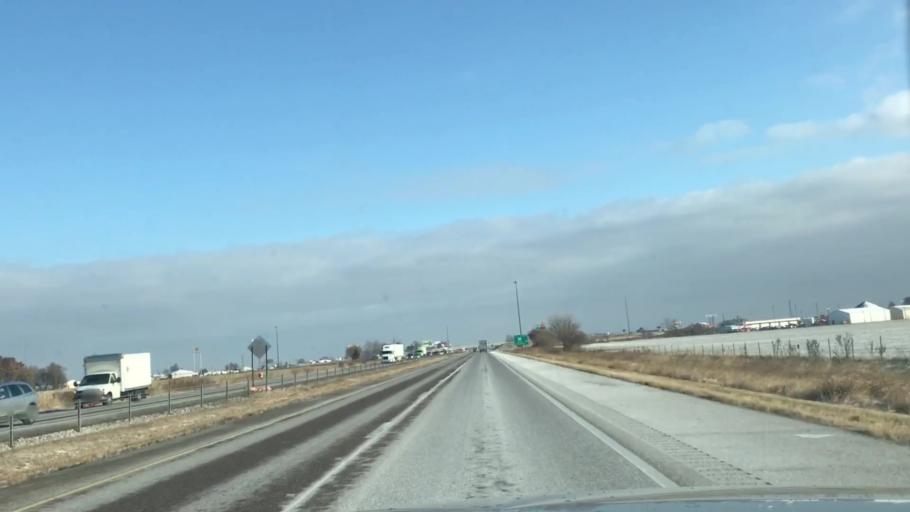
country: US
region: Illinois
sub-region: Madison County
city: Worden
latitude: 38.8829
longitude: -89.8423
